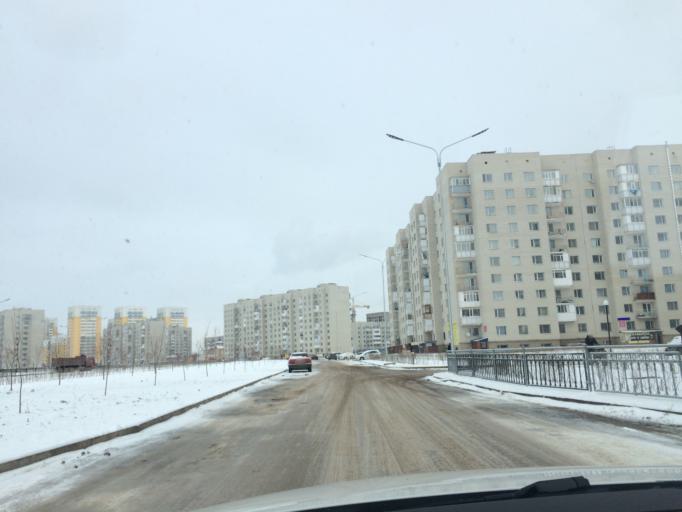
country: KZ
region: Astana Qalasy
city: Astana
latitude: 51.1230
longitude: 71.5047
